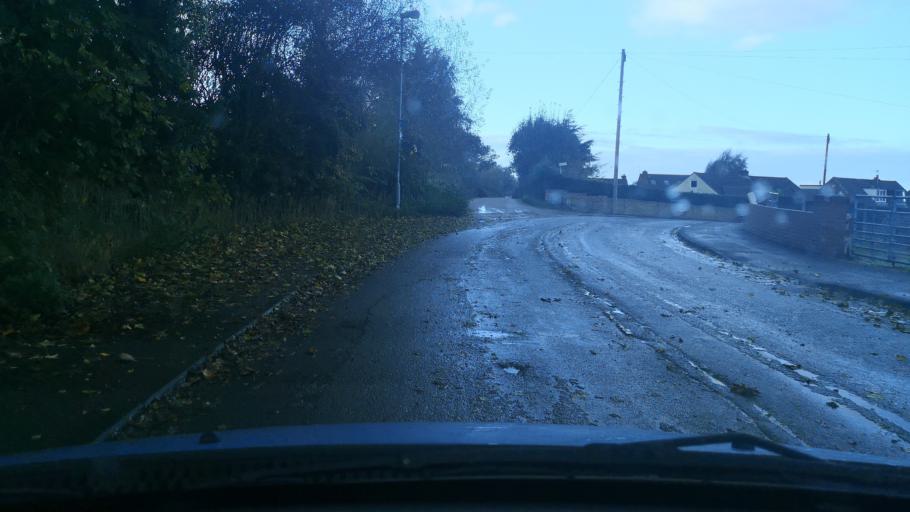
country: GB
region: England
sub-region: City and Borough of Wakefield
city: Crigglestone
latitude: 53.6288
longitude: -1.5256
